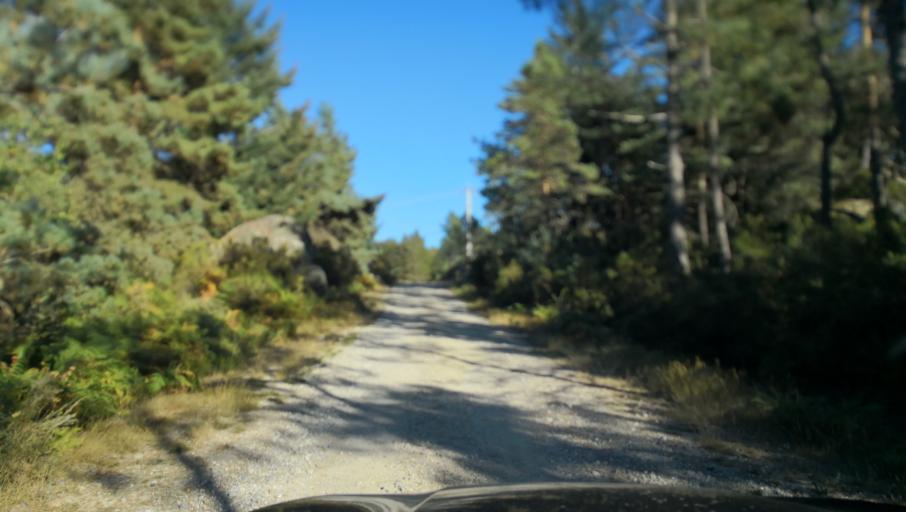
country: PT
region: Vila Real
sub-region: Vila Real
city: Vila Real
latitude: 41.3534
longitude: -7.7911
